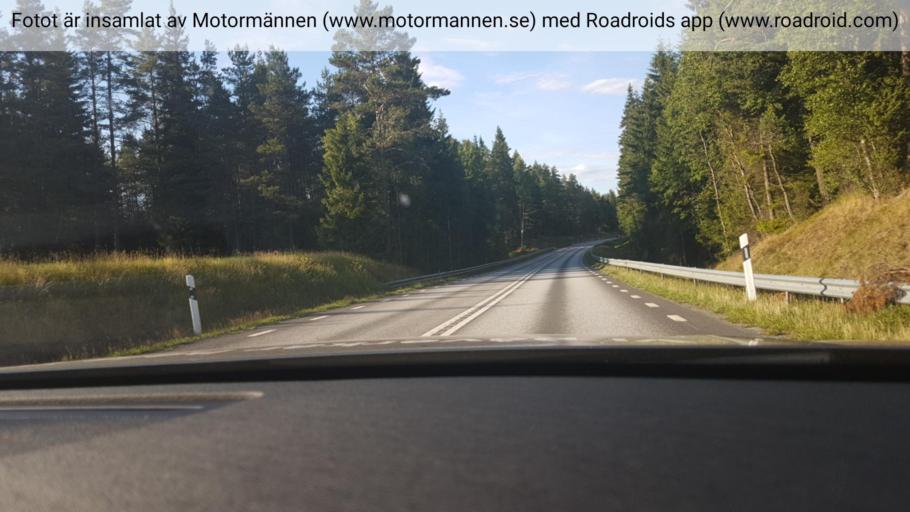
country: SE
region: Joenkoeping
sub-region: Mullsjo Kommun
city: Mullsjoe
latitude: 57.7201
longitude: 13.8581
